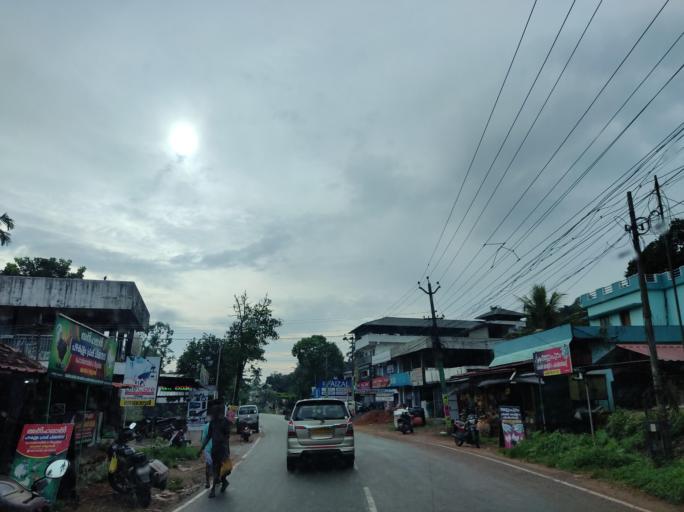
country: IN
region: Kerala
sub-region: Pattanamtitta
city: Adur
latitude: 9.1658
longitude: 76.6835
